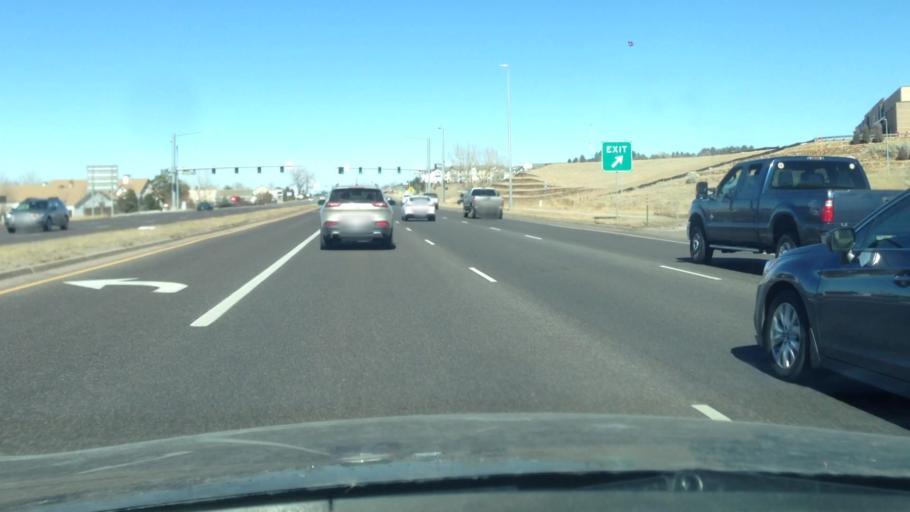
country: US
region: Colorado
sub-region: Douglas County
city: Stonegate
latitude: 39.5532
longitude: -104.7769
